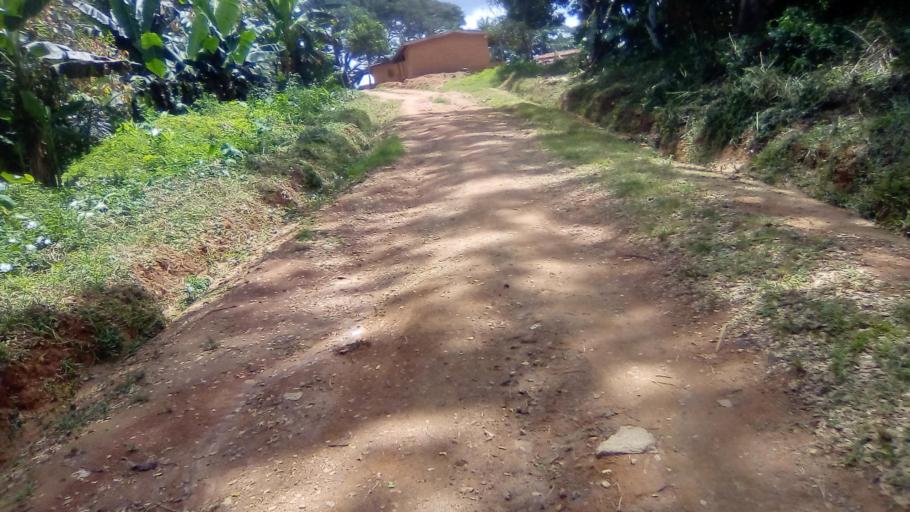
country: SL
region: Eastern Province
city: Giehun
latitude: 8.4968
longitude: -10.9080
